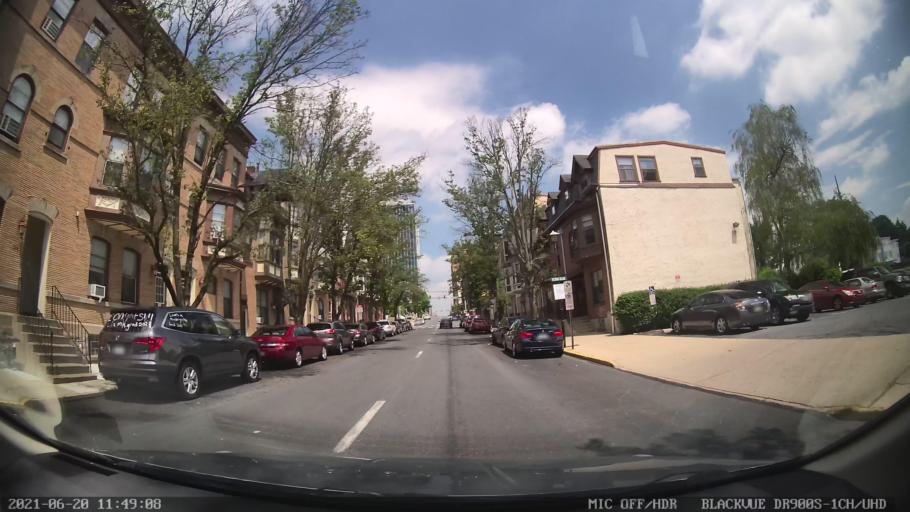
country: US
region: Pennsylvania
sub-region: Lehigh County
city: Allentown
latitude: 40.6006
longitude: -75.4687
